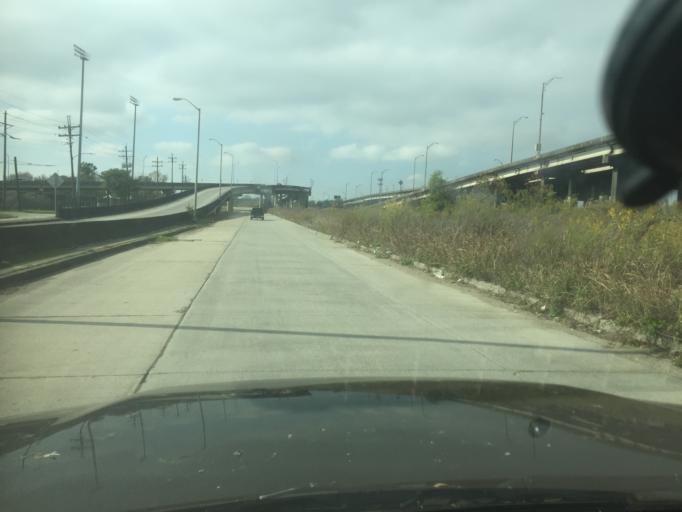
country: US
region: Louisiana
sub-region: Saint Bernard Parish
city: Arabi
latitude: 30.0030
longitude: -90.0323
